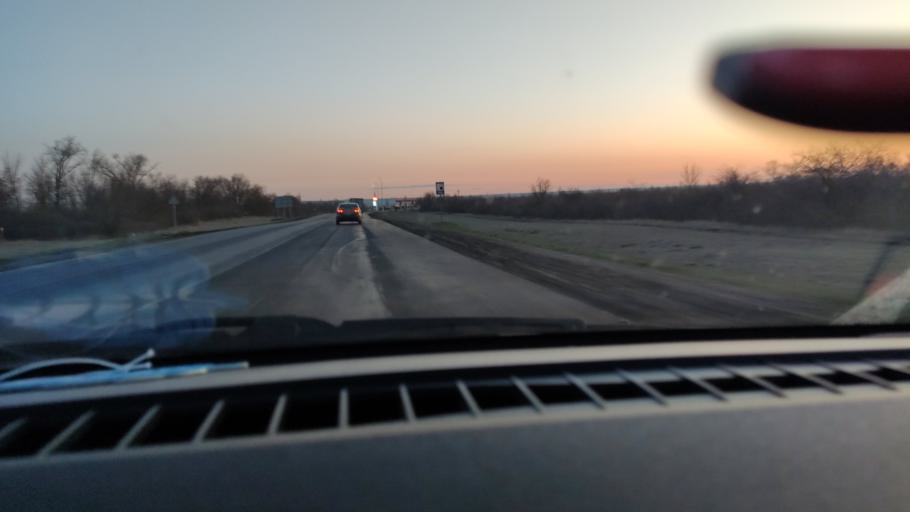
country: RU
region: Saratov
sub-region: Saratovskiy Rayon
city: Saratov
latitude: 51.6777
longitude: 46.0011
